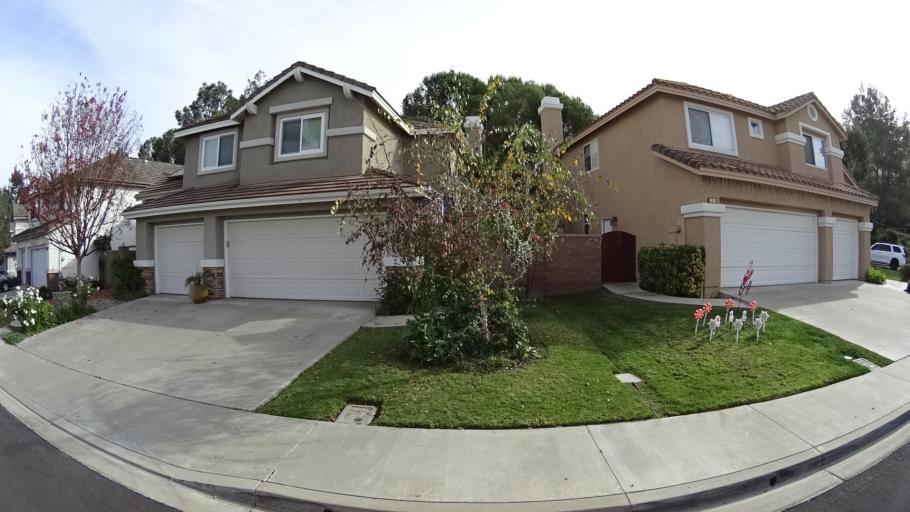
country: US
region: California
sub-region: Orange County
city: Laguna Woods
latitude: 33.6008
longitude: -117.7369
